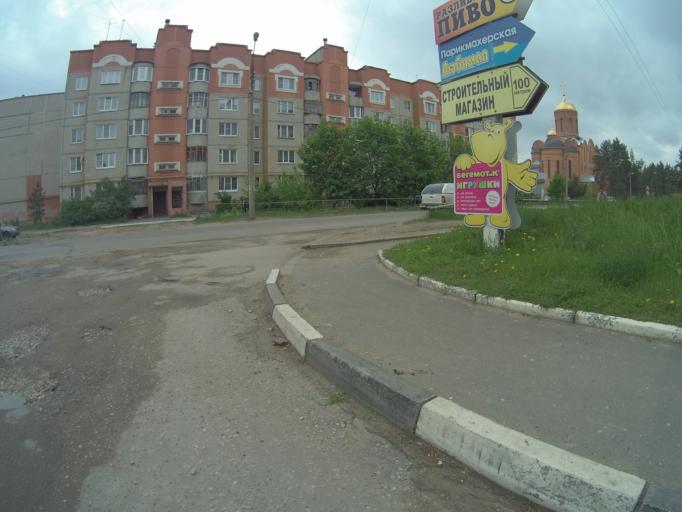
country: RU
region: Vladimir
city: Kommunar
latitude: 56.1061
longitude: 40.4416
